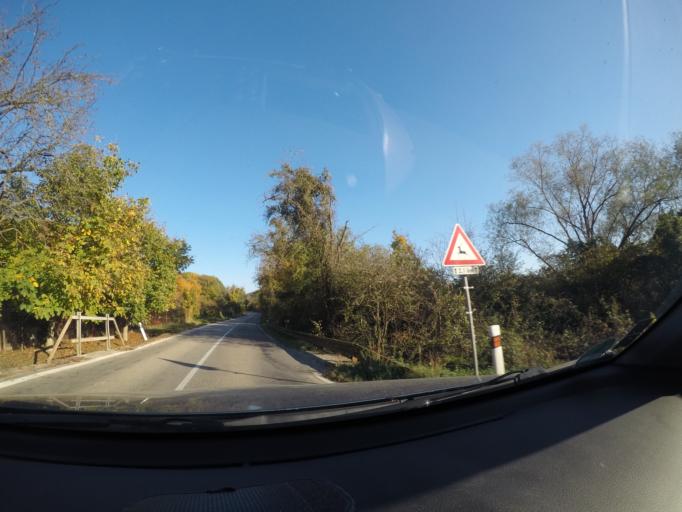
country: SK
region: Trenciansky
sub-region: Okres Trencin
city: Trencin
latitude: 48.9050
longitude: 18.0659
